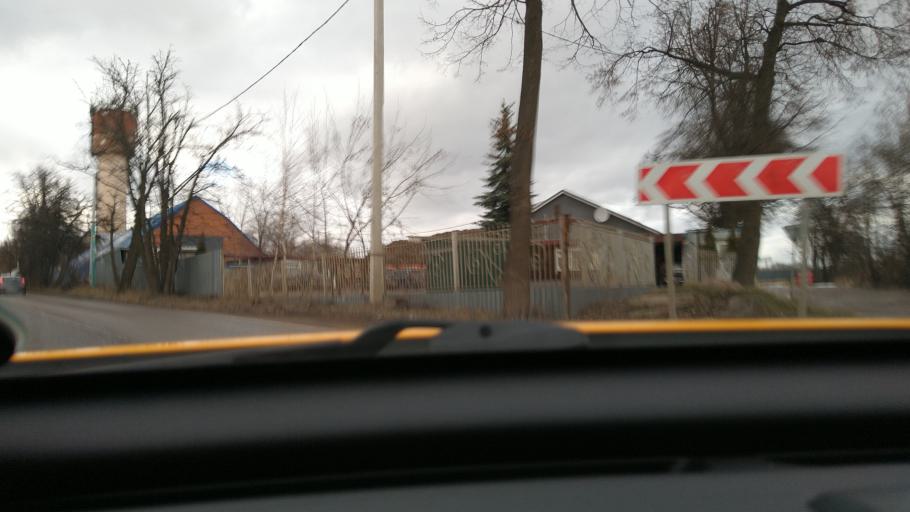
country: RU
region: Moskovskaya
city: Petrovo-Dal'neye
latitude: 55.7705
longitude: 37.2227
